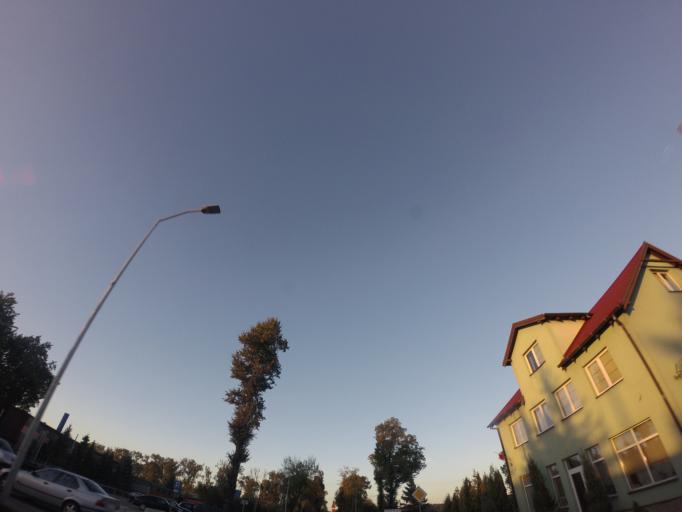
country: PL
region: Lubusz
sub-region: Powiat strzelecko-drezdenecki
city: Drezdenko
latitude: 52.8480
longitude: 15.8353
